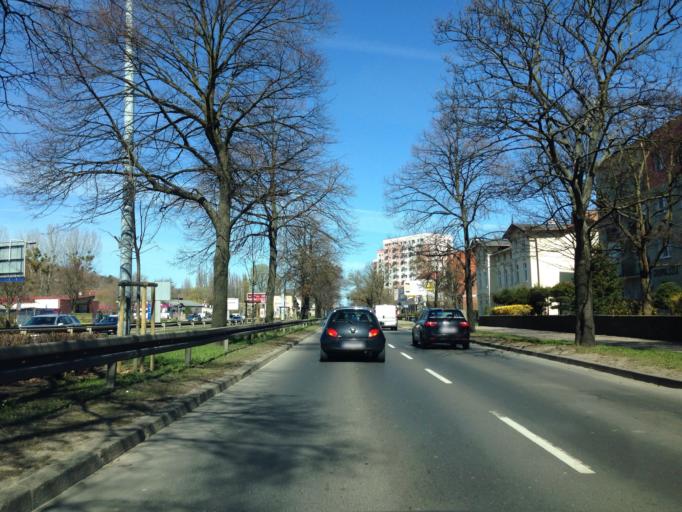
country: PL
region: Pomeranian Voivodeship
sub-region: Sopot
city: Sopot
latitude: 54.4165
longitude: 18.5660
